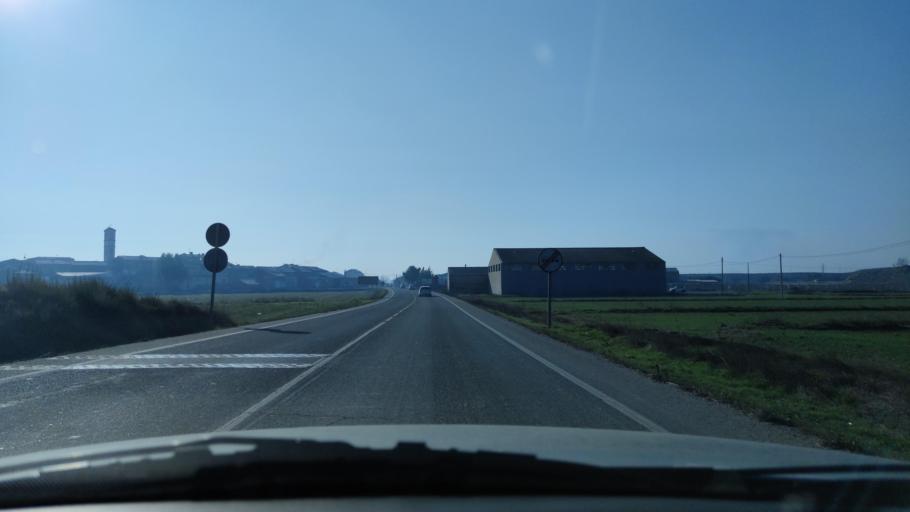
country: ES
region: Catalonia
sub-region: Provincia de Lleida
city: Torrefarrera
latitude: 41.6753
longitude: 0.6296
